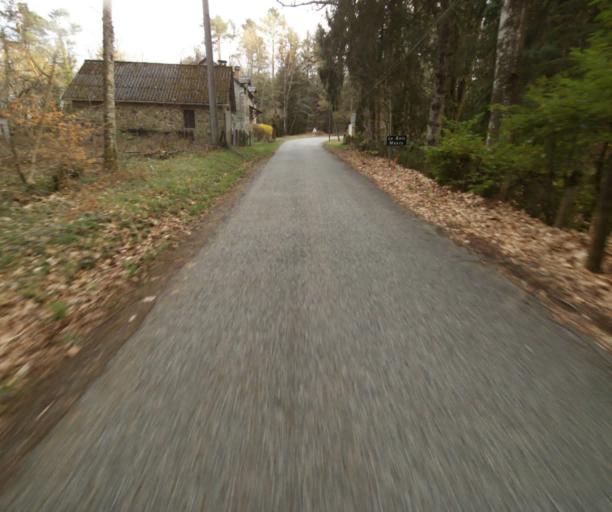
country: FR
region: Limousin
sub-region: Departement de la Correze
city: Argentat
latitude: 45.2191
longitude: 1.9710
